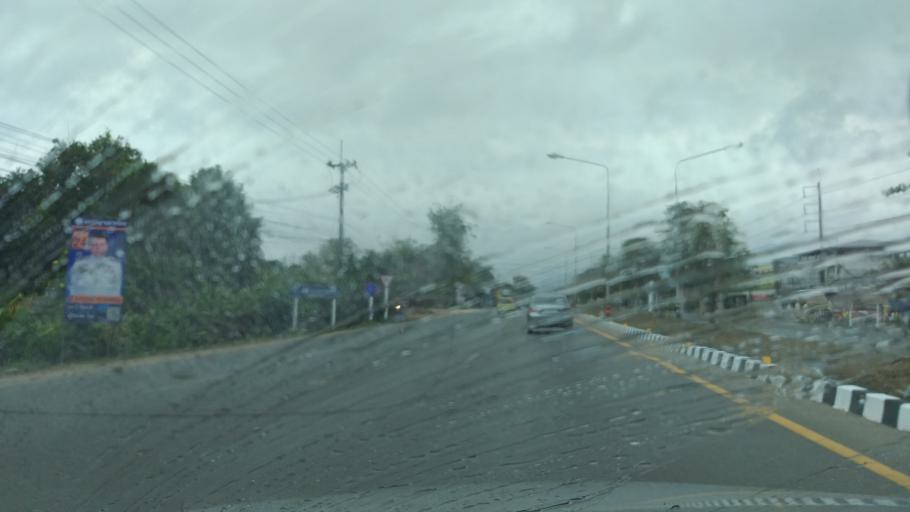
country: TH
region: Chanthaburi
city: Khlung
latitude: 12.4533
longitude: 102.2412
